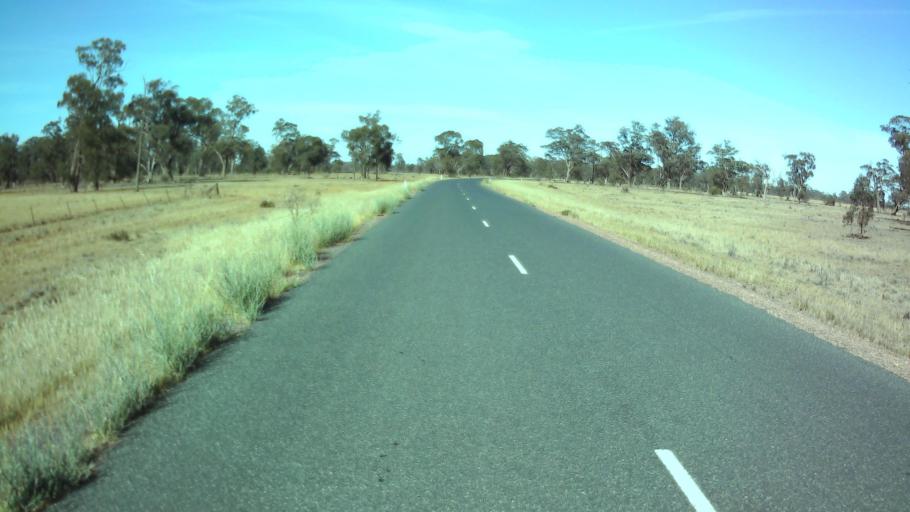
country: AU
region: New South Wales
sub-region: Weddin
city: Grenfell
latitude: -34.1115
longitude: 147.8503
